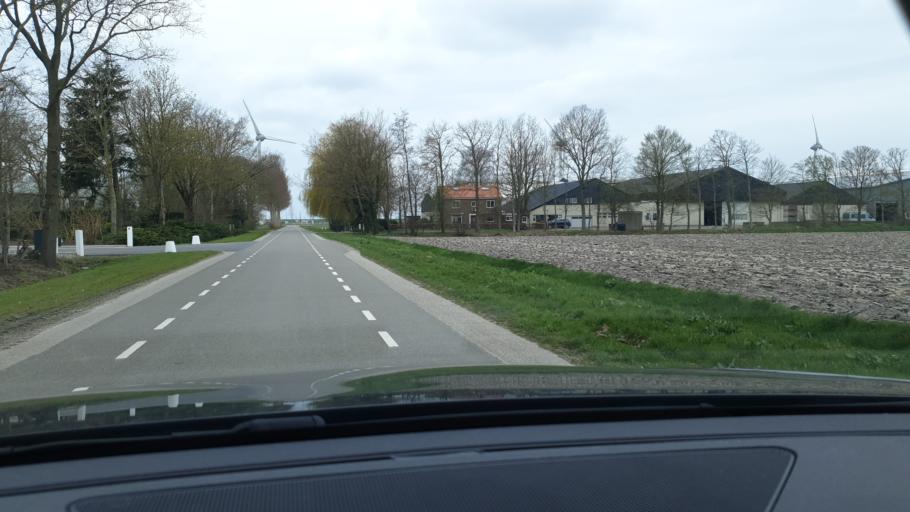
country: NL
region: Flevoland
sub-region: Gemeente Urk
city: Urk
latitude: 52.7254
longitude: 5.6140
